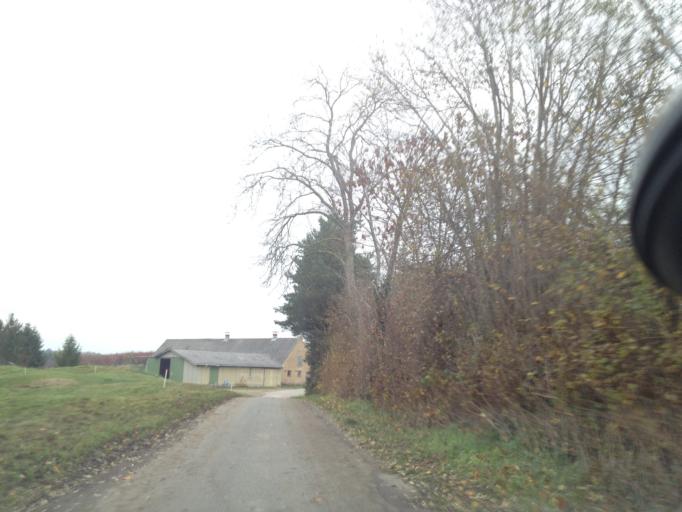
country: DK
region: South Denmark
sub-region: Nordfyns Kommune
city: Sonderso
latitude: 55.4250
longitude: 10.2163
